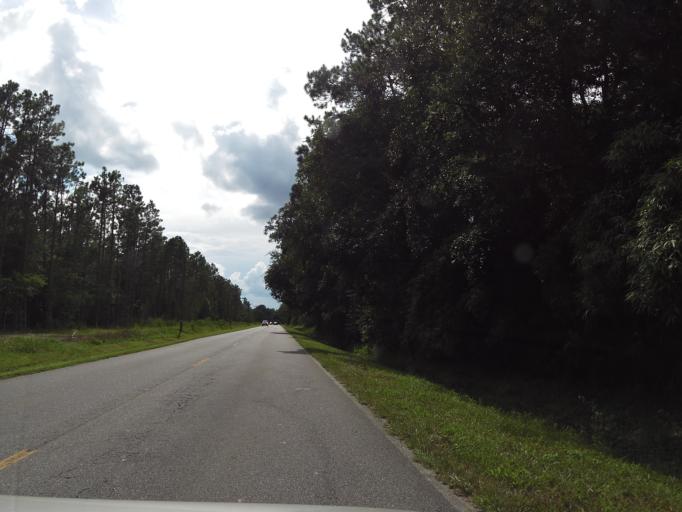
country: US
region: Florida
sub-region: Clay County
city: Green Cove Springs
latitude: 30.0218
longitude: -81.7237
